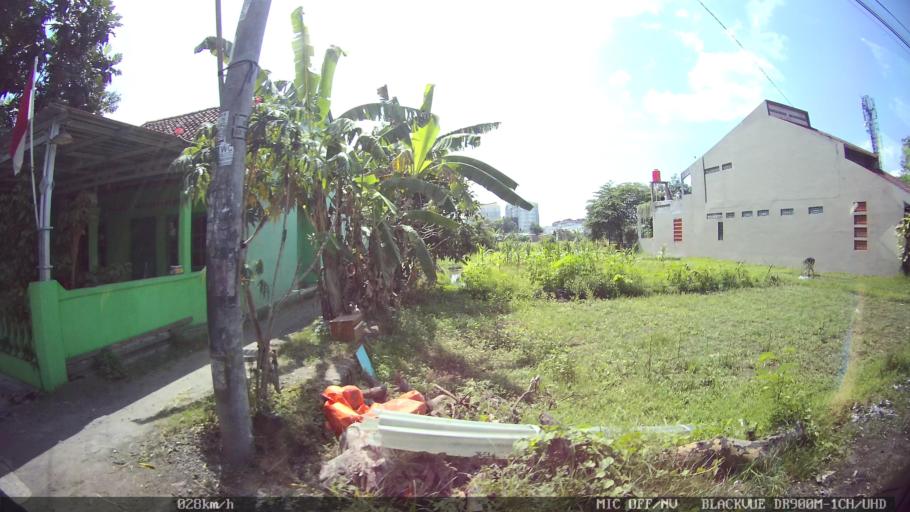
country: ID
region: Daerah Istimewa Yogyakarta
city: Sewon
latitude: -7.8331
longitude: 110.3786
